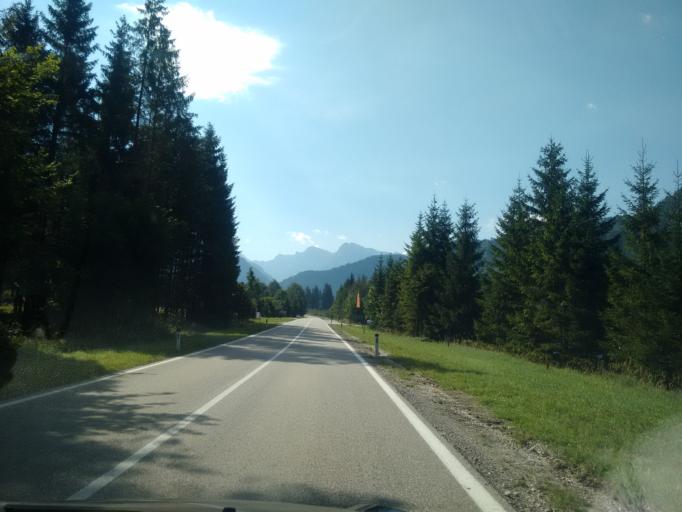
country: AT
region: Upper Austria
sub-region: Politischer Bezirk Gmunden
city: Gruenau im Almtal
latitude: 47.8079
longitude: 13.9512
